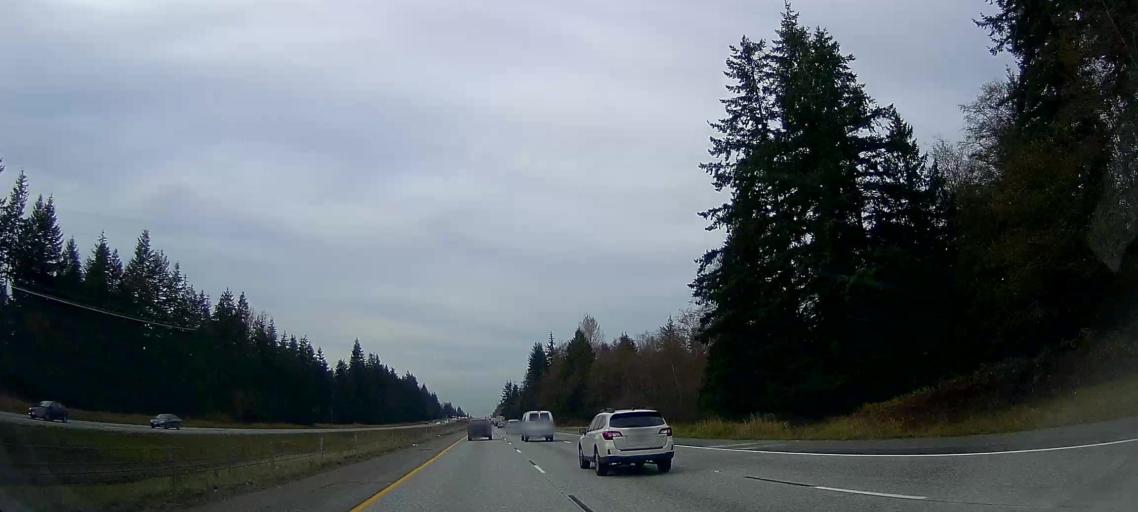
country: US
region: Washington
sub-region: Snohomish County
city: Stanwood
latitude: 48.2842
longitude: -122.2877
